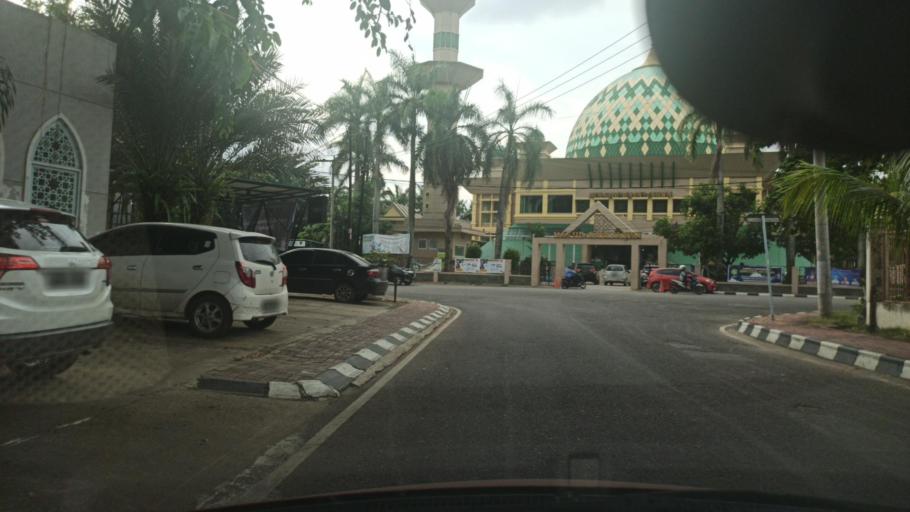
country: ID
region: South Sumatra
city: Plaju
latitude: -2.9888
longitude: 104.7441
